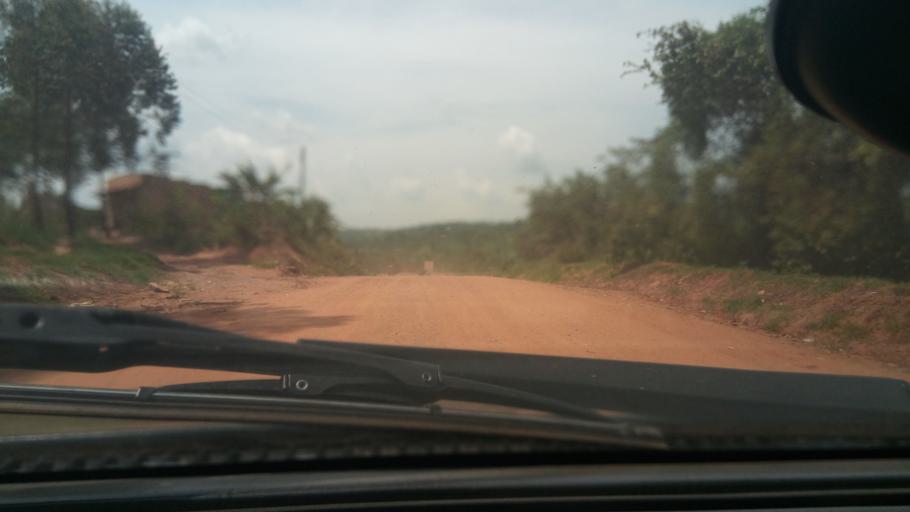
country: UG
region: Central Region
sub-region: Mityana District
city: Mityana
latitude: 0.4149
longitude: 32.0494
